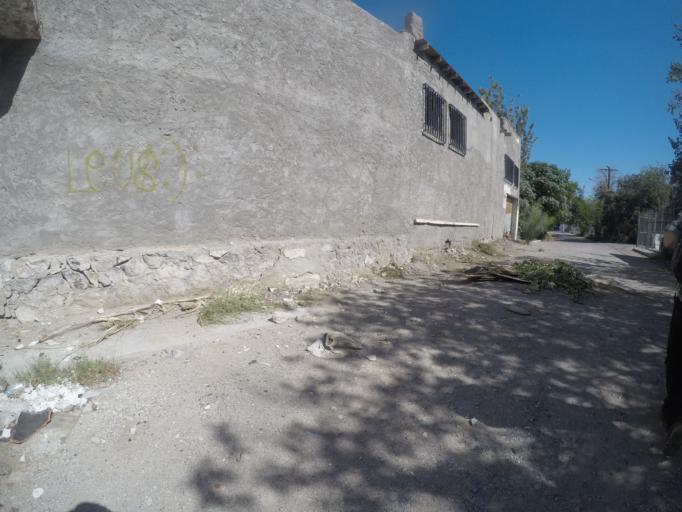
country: MX
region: Chihuahua
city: Ciudad Juarez
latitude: 31.7391
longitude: -106.4749
